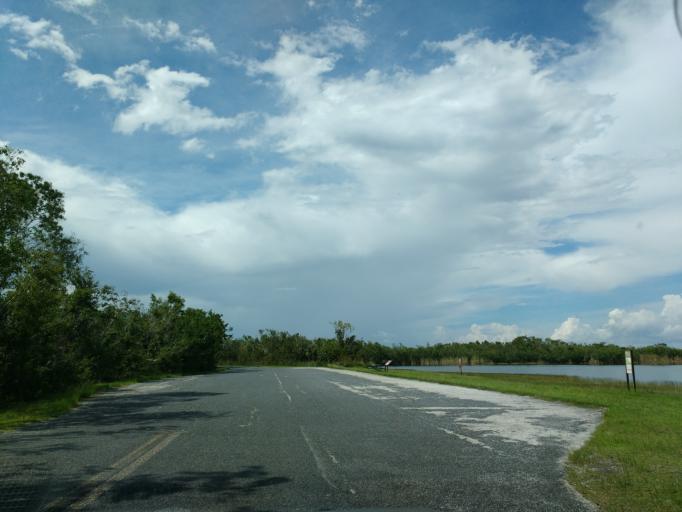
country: US
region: Florida
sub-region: Monroe County
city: Plantation
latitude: 25.2534
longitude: -80.7981
